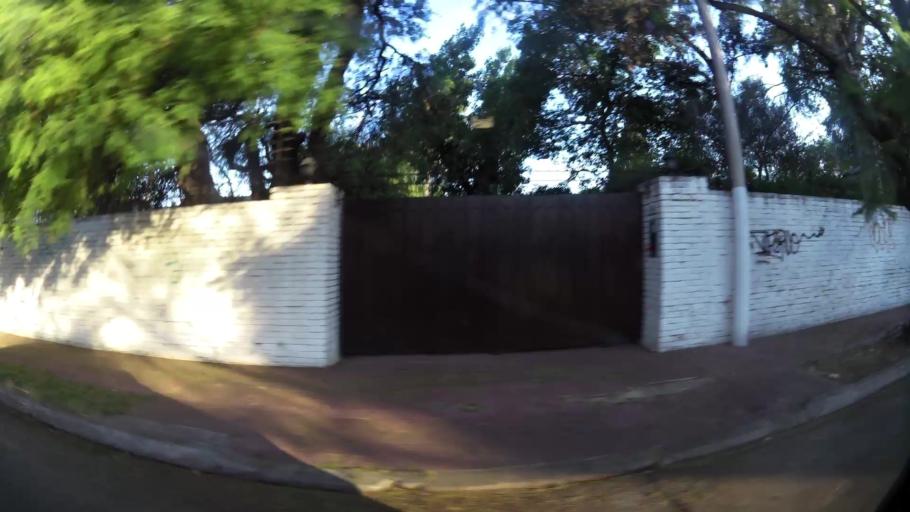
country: AR
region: Cordoba
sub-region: Departamento de Capital
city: Cordoba
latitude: -31.3781
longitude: -64.2389
